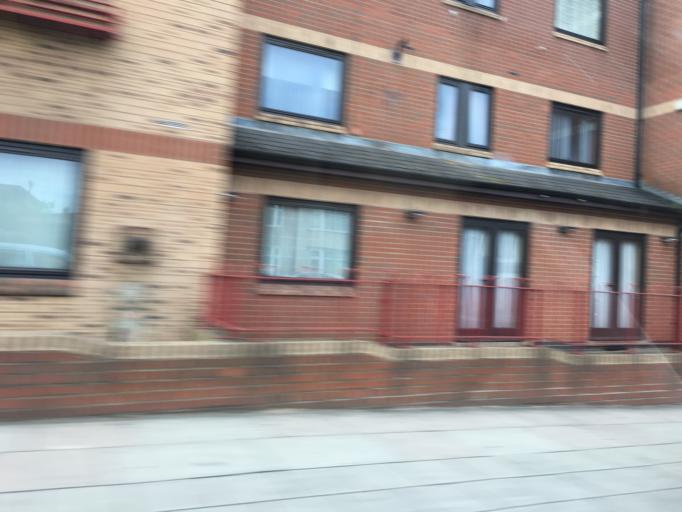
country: GB
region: England
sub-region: City of Leicester
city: Leicester
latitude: 52.6291
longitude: -1.1072
